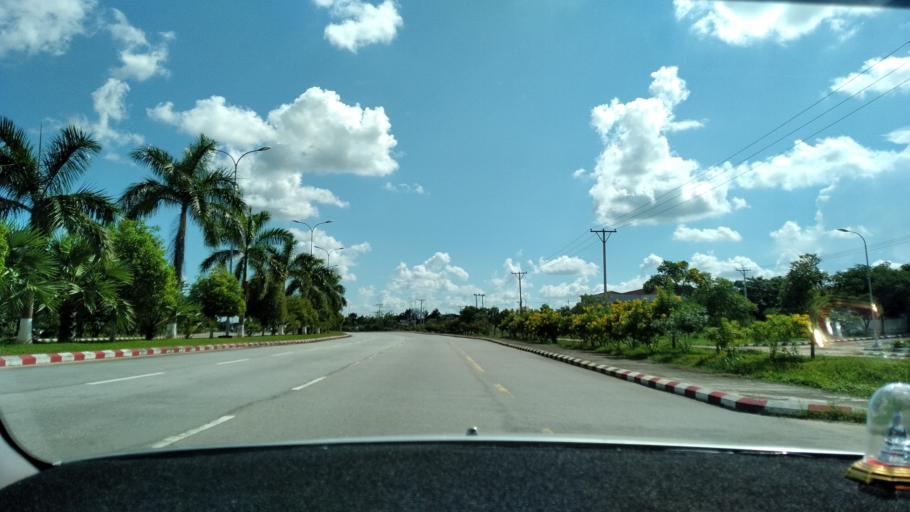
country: MM
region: Mandalay
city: Nay Pyi Taw
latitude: 19.7798
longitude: 96.1432
